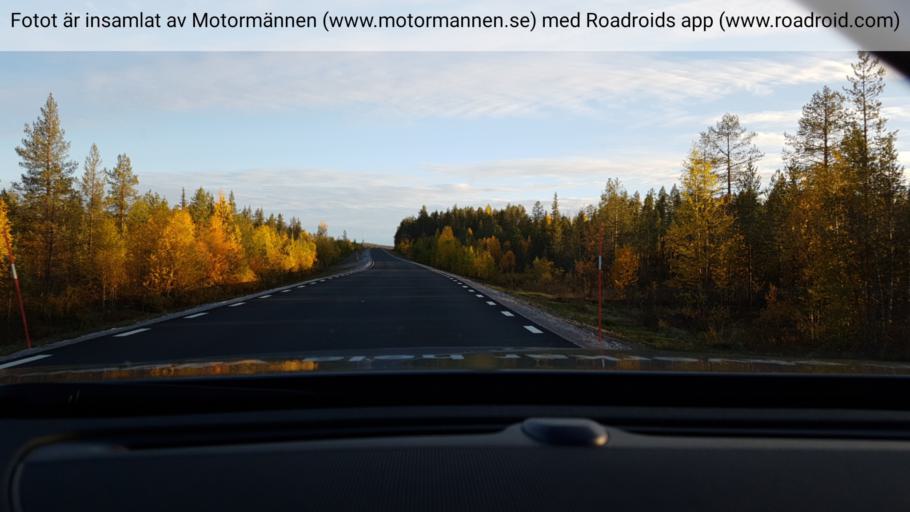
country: SE
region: Norrbotten
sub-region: Jokkmokks Kommun
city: Jokkmokk
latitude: 66.5872
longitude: 19.8027
